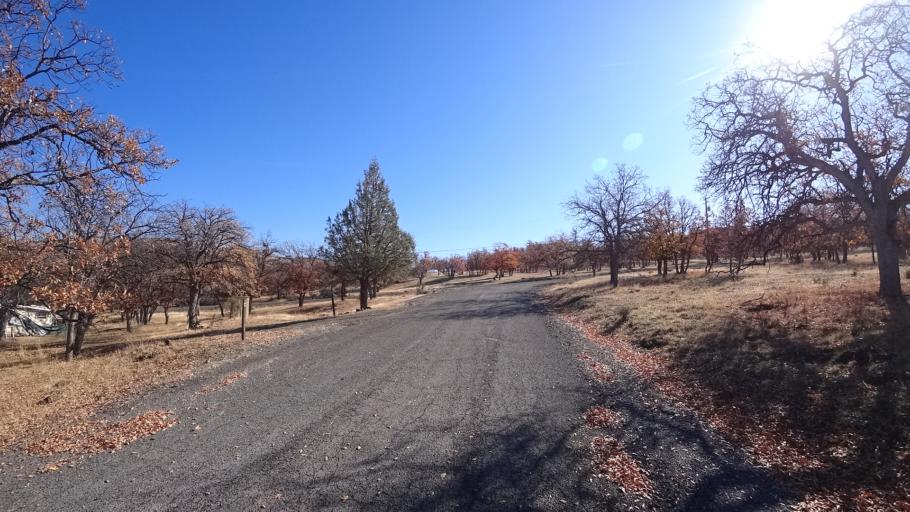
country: US
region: California
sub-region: Siskiyou County
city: Montague
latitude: 41.8853
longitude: -122.4845
